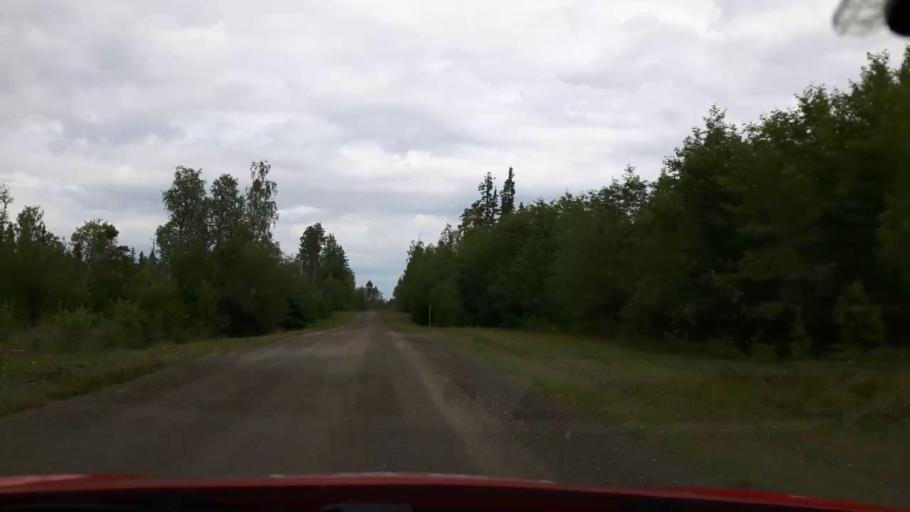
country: SE
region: Jaemtland
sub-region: Stroemsunds Kommun
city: Stroemsund
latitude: 63.7988
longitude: 15.6145
